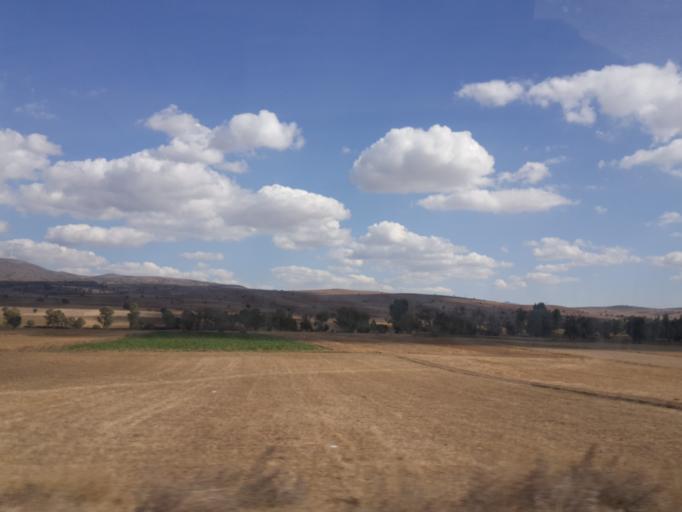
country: TR
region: Tokat
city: Camlibel
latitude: 40.1852
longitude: 36.4527
